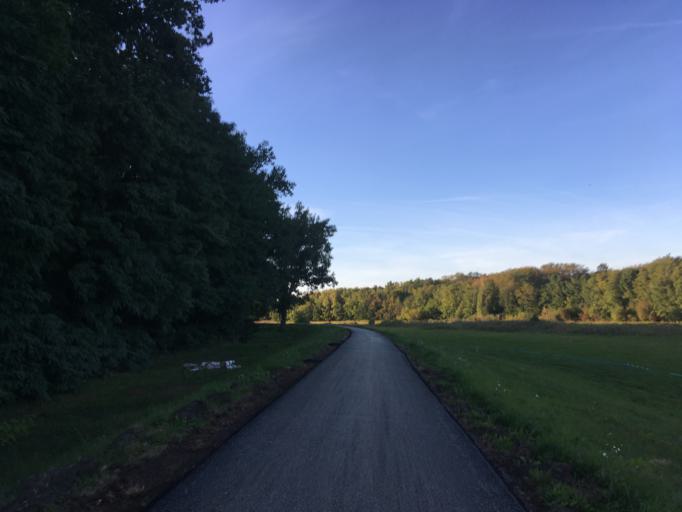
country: DE
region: Brandenburg
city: Forst
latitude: 51.7210
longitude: 14.6776
